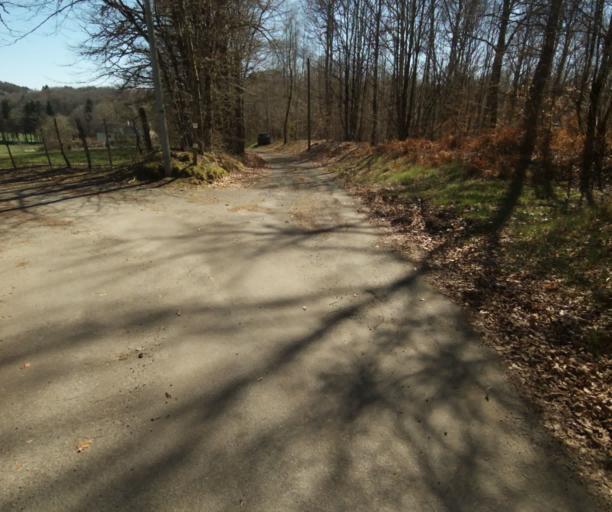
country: FR
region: Limousin
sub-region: Departement de la Correze
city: Chamboulive
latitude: 45.4554
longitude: 1.7290
